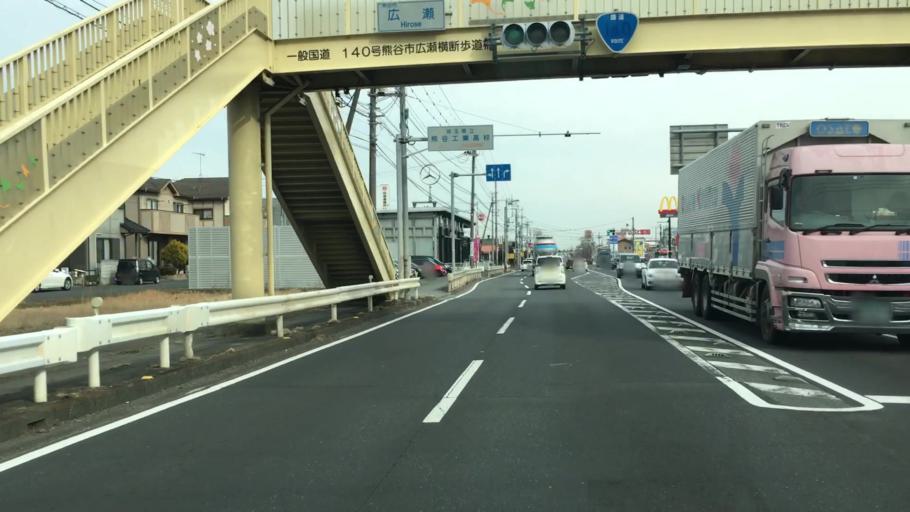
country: JP
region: Saitama
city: Kumagaya
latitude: 36.1525
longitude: 139.3570
